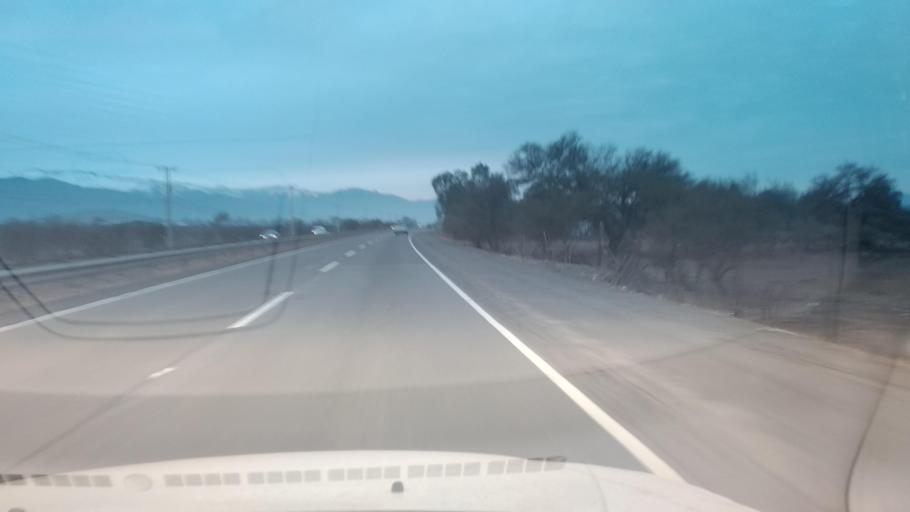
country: CL
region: Santiago Metropolitan
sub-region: Provincia de Chacabuco
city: Chicureo Abajo
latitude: -33.1260
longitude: -70.6741
